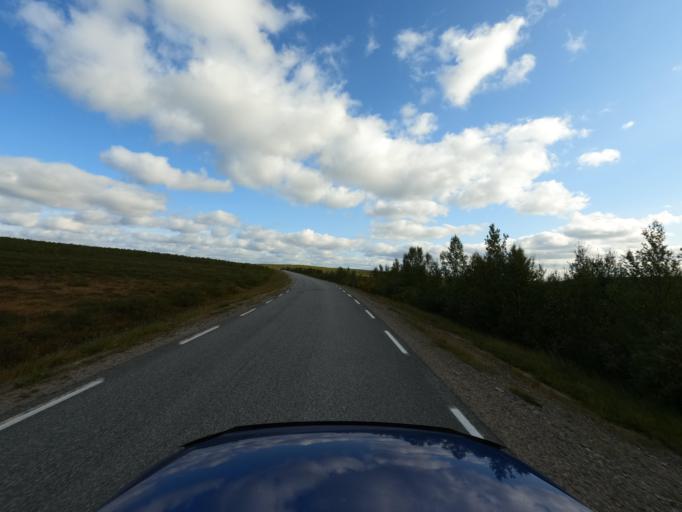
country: NO
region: Finnmark Fylke
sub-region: Porsanger
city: Lakselv
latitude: 69.3741
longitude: 24.4222
